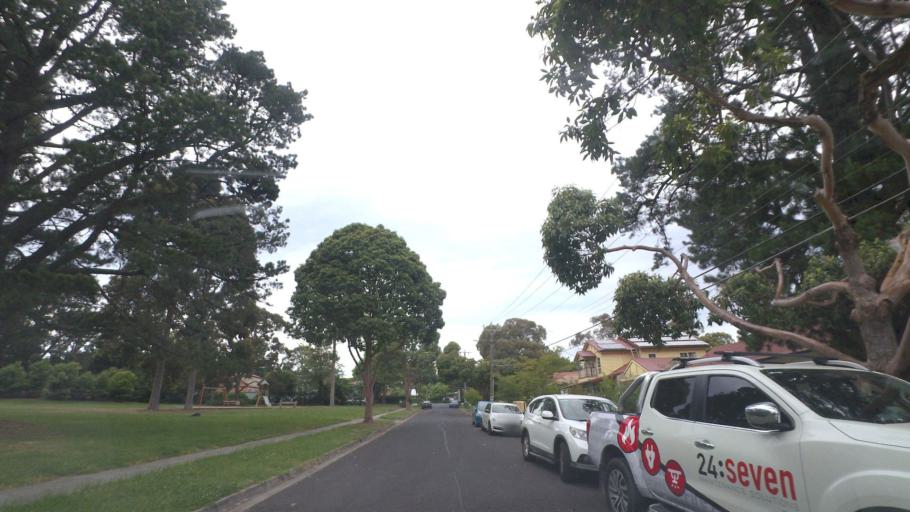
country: AU
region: Victoria
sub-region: Maroondah
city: Croydon Hills
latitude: -37.7928
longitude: 145.2669
